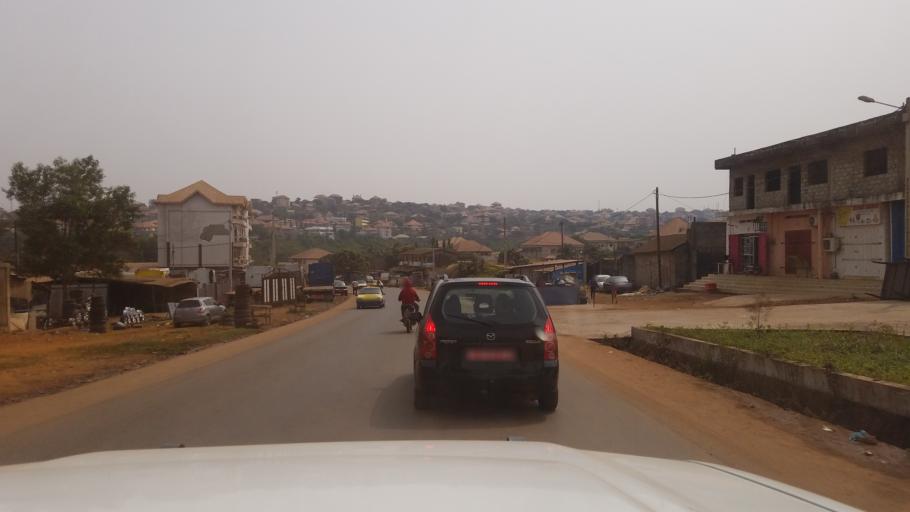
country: GN
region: Conakry
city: Conakry
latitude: 9.6462
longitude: -13.6058
